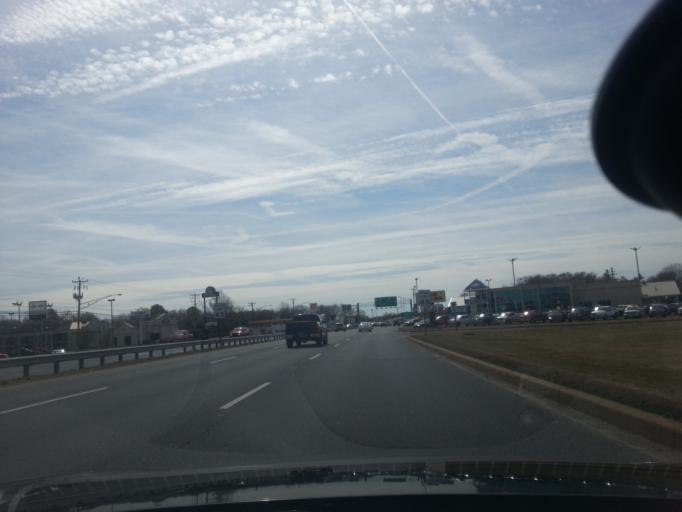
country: US
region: Maryland
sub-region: Wicomico County
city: Delmar
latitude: 38.4093
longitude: -75.5678
